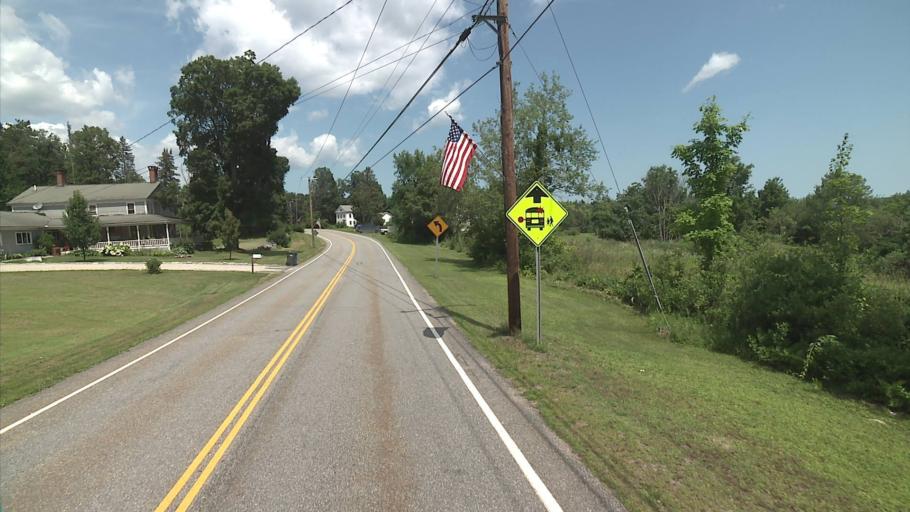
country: US
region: Connecticut
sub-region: Litchfield County
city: Winsted
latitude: 42.0052
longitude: -72.9720
